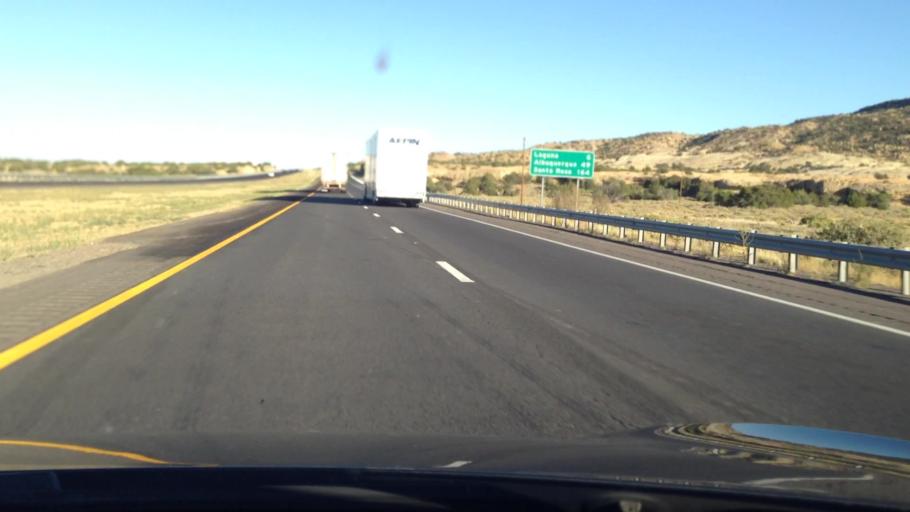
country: US
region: New Mexico
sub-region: Cibola County
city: Laguna
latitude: 35.0308
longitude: -107.4629
